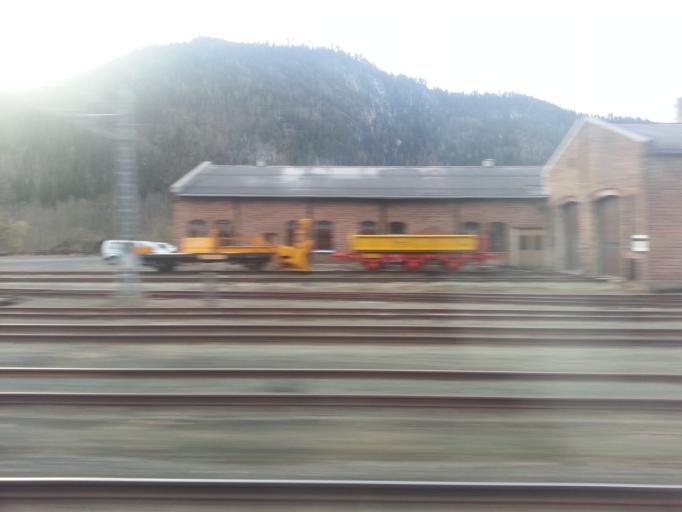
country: NO
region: Sor-Trondelag
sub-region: Midtre Gauldal
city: Storen
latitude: 63.0554
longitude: 10.2858
